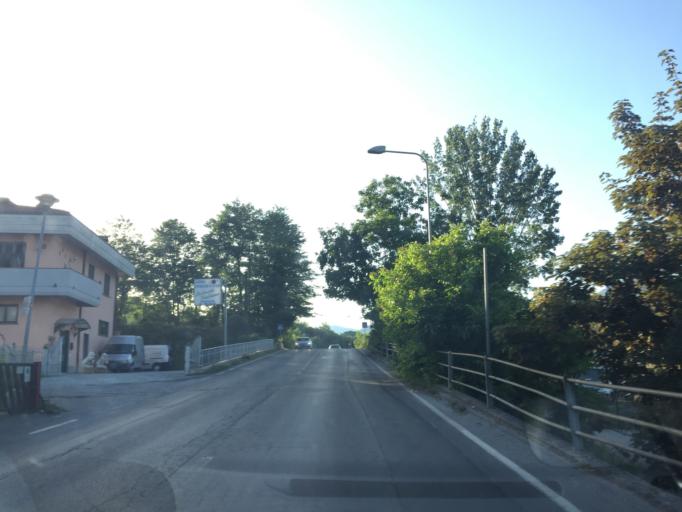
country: IT
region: Tuscany
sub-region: Provincia di Lucca
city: Castelnuovo di Garfagnana
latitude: 44.1144
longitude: 10.4027
